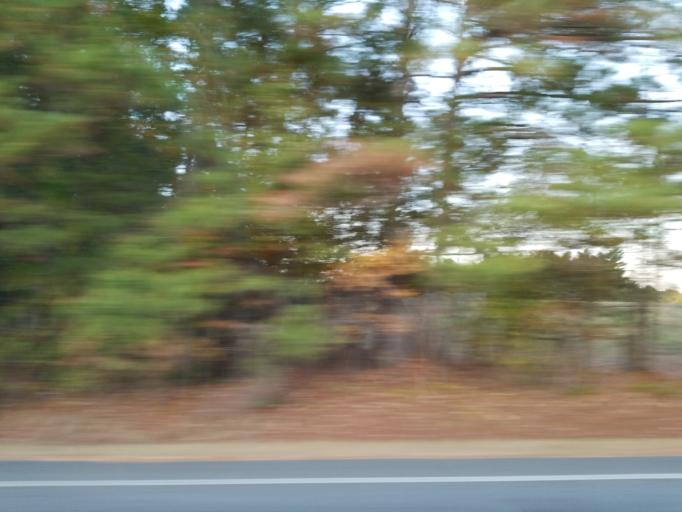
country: US
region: Georgia
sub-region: Gordon County
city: Calhoun
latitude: 34.5919
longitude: -85.0220
